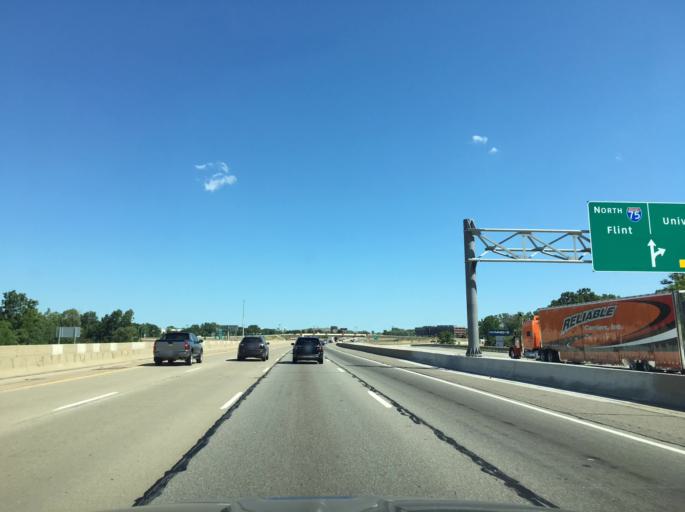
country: US
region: Michigan
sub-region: Oakland County
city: Auburn Hills
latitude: 42.6600
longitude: -83.2403
